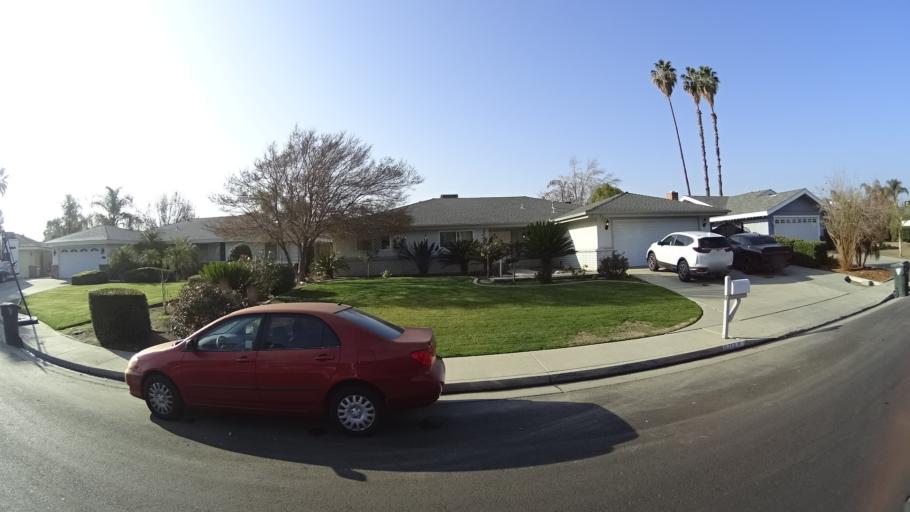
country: US
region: California
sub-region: Kern County
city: Greenacres
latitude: 35.3304
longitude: -119.0709
